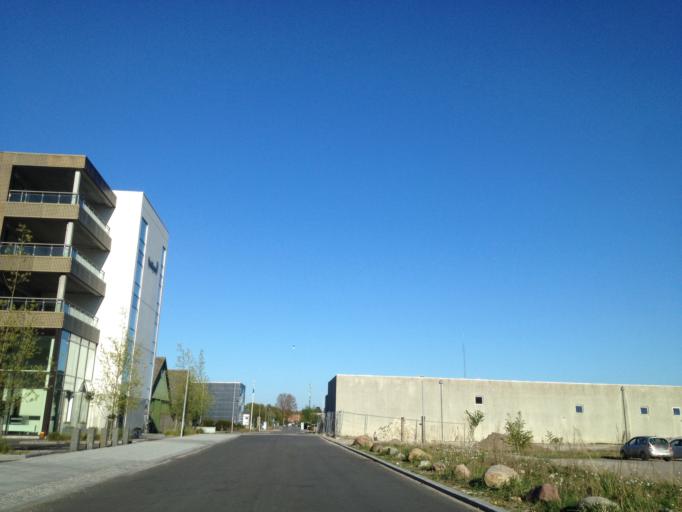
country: DK
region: Zealand
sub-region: Holbaek Kommune
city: Holbaek
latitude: 55.7195
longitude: 11.7191
